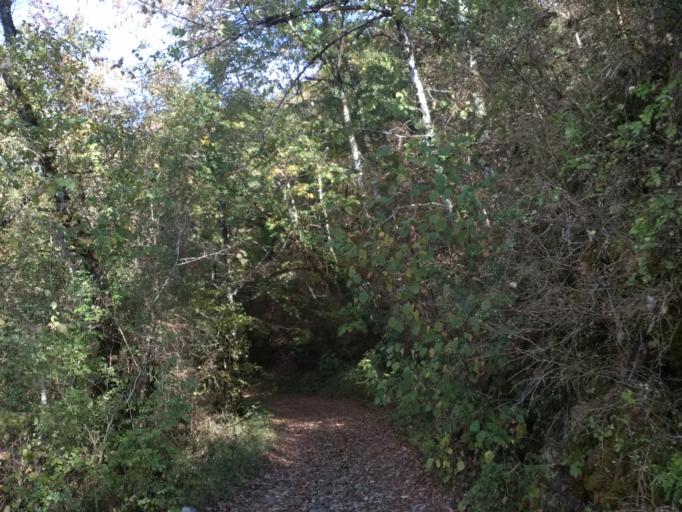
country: FR
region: Midi-Pyrenees
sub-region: Departement de l'Aveyron
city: Bozouls
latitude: 44.4798
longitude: 2.6733
